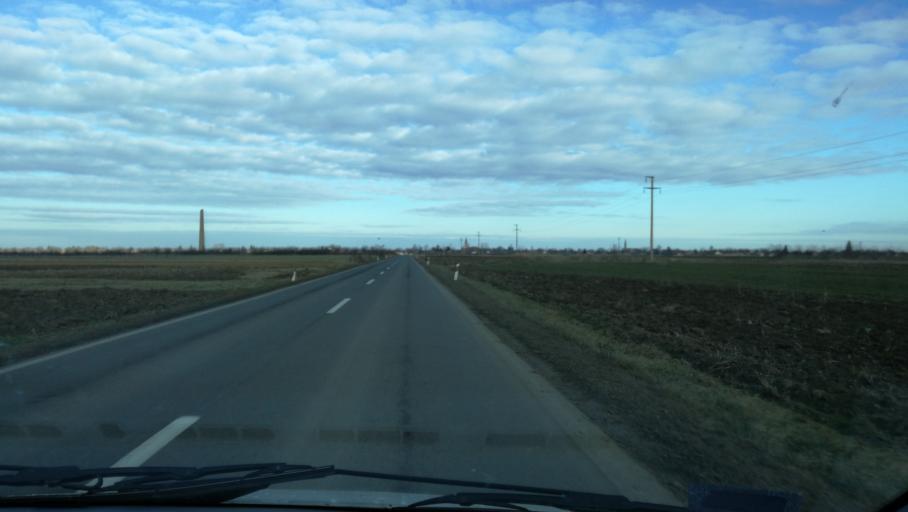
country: RS
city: Ostojicevo
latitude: 45.8756
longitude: 20.1650
